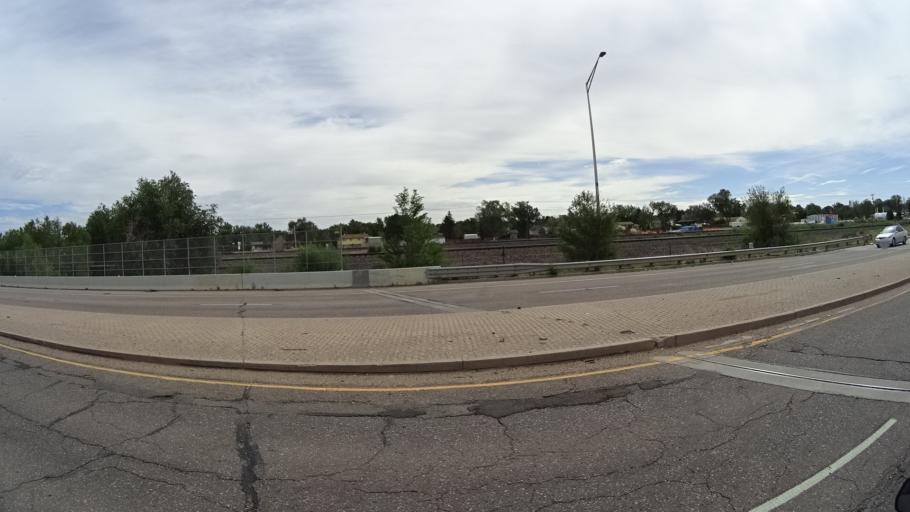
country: US
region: Colorado
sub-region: El Paso County
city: Security-Widefield
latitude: 38.7289
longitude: -104.7238
